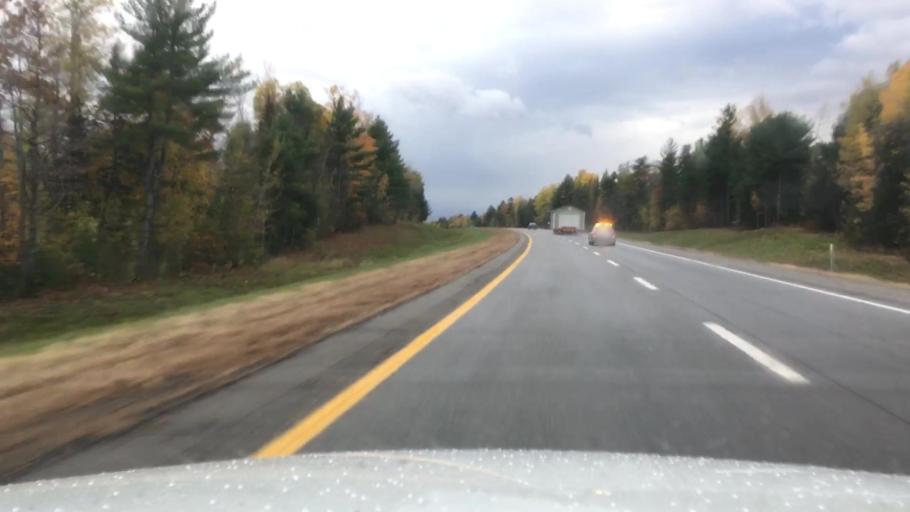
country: US
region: Maine
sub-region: Penobscot County
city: Howland
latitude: 45.2629
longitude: -68.6808
